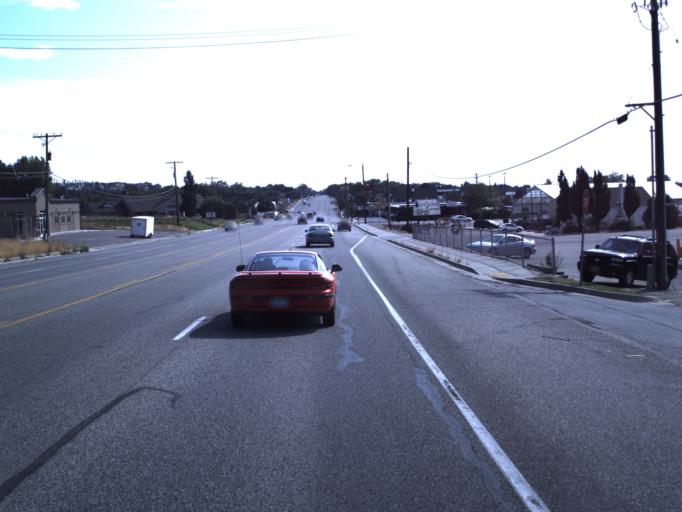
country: US
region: Utah
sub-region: Box Elder County
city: Perry
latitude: 41.4780
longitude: -112.0228
